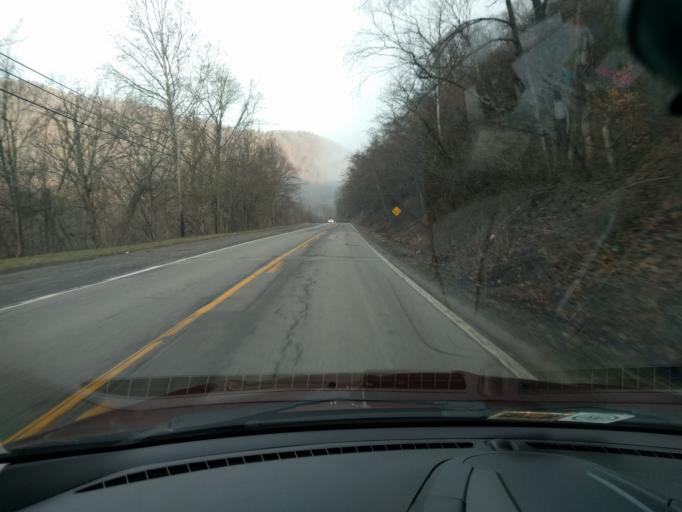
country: US
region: West Virginia
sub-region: Kanawha County
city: Montgomery
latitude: 38.1595
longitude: -81.2973
